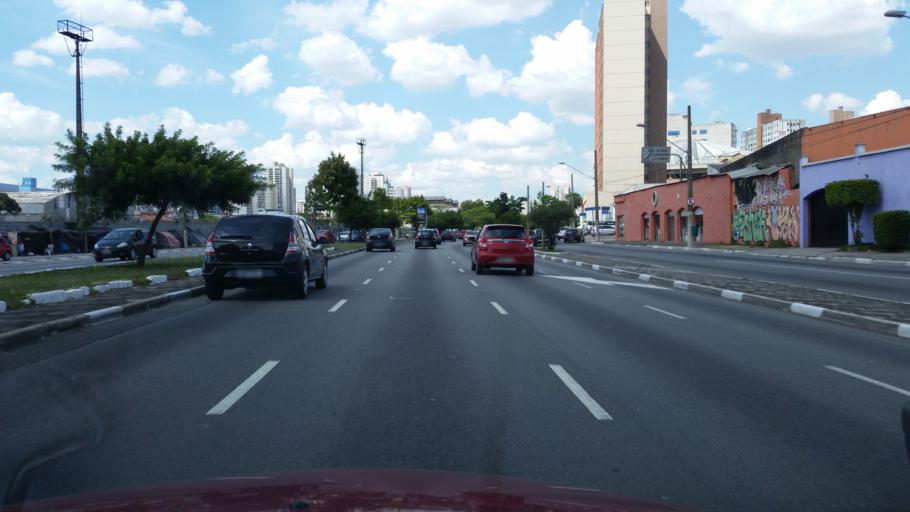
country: BR
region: Sao Paulo
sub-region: Sao Paulo
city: Sao Paulo
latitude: -23.5461
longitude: -46.5989
